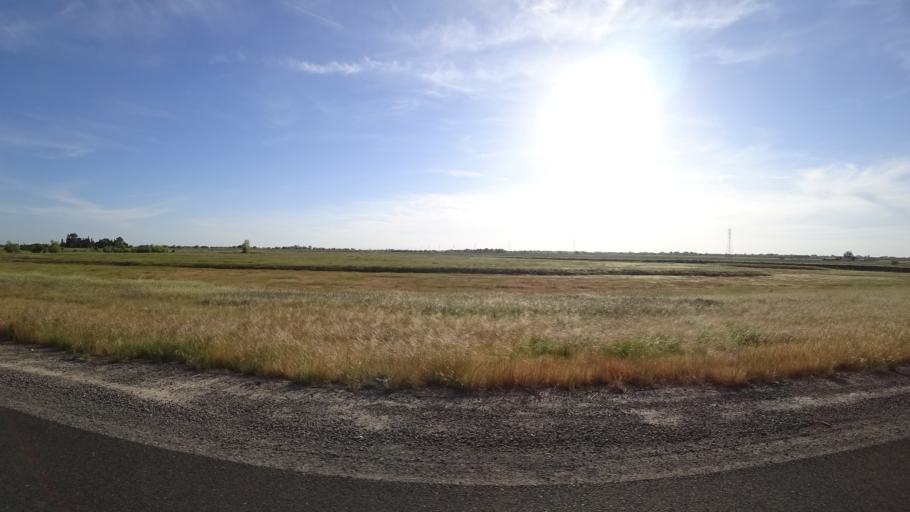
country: US
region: California
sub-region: Placer County
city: Sheridan
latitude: 38.9833
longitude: -121.3845
